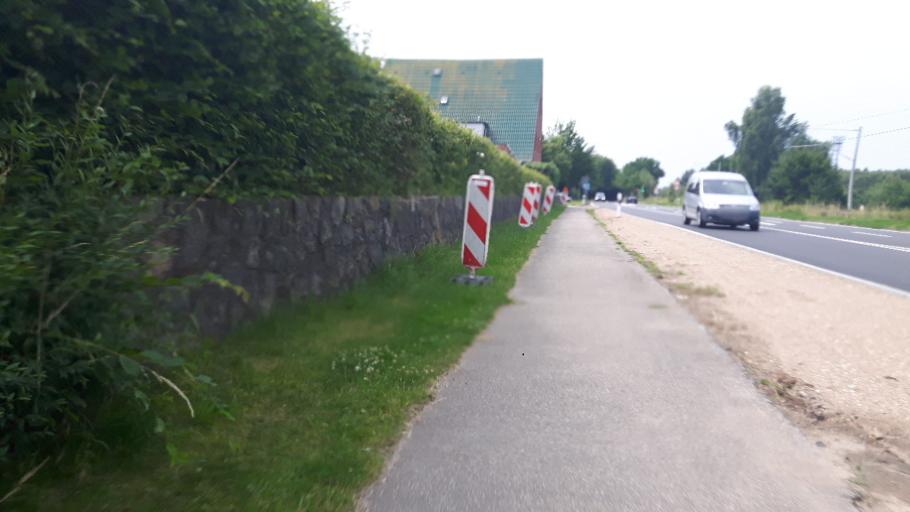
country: DE
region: Mecklenburg-Vorpommern
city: Selmsdorf
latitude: 53.9261
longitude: 10.8219
